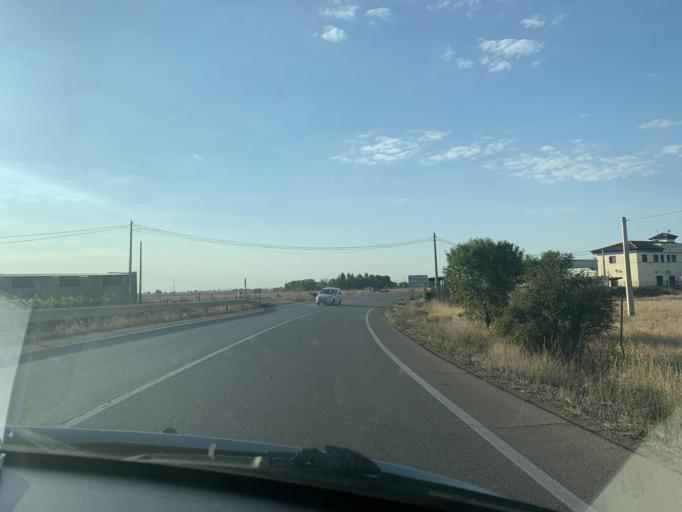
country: ES
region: Castille-La Mancha
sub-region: Provincia de Ciudad Real
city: Argamasilla de Alba
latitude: 39.1703
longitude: -3.2305
